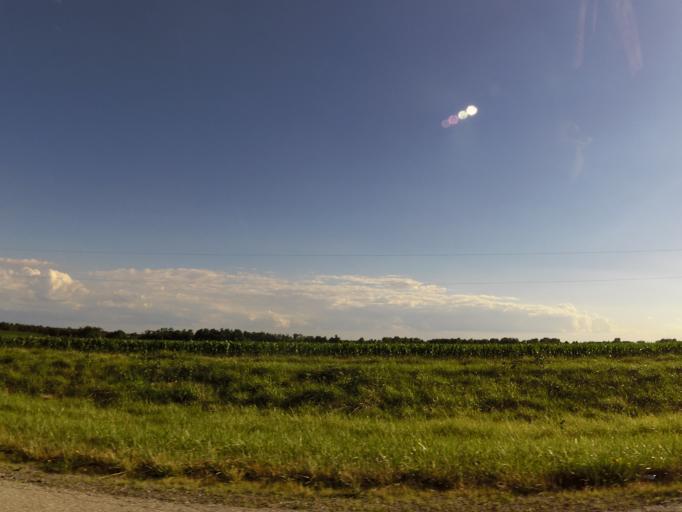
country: US
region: Missouri
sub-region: Pike County
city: Bowling Green
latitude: 39.3137
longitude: -91.1387
